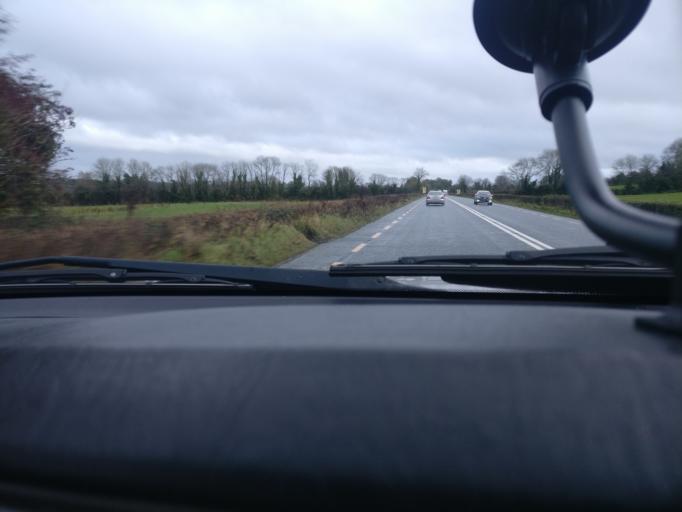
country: IE
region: Leinster
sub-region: An Mhi
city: Enfield
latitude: 53.4212
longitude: -6.7606
